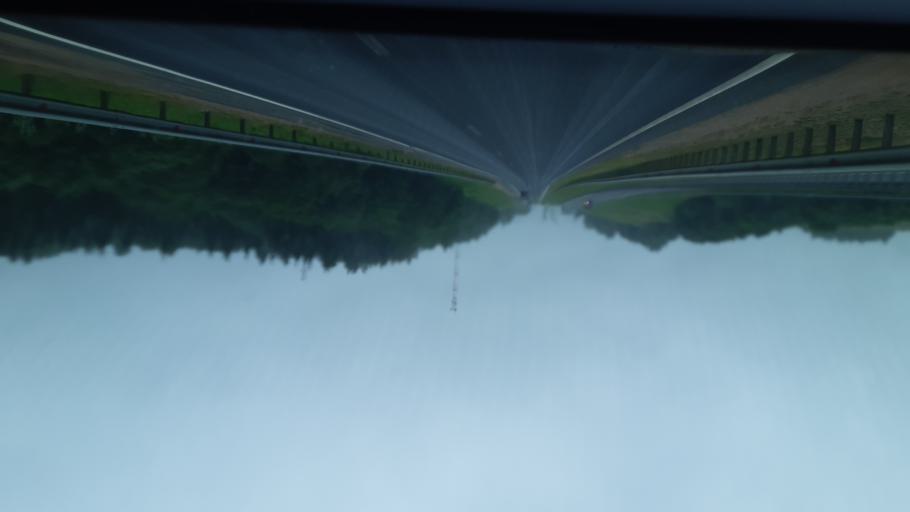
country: RU
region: Smolensk
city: Talashkino
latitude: 54.6337
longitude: 32.1835
